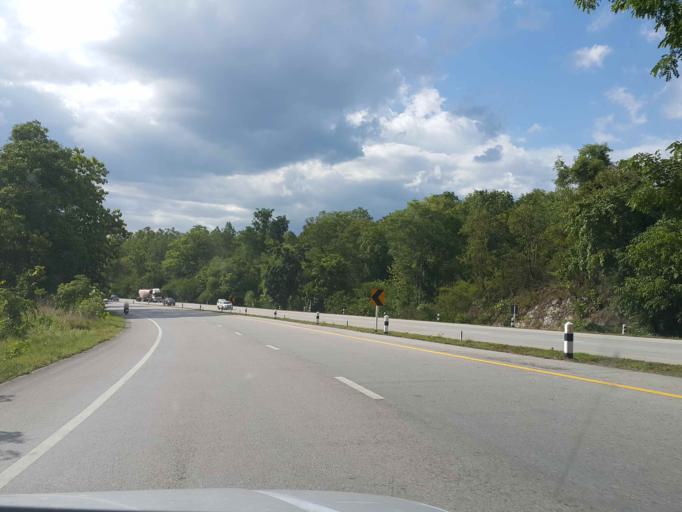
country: TH
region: Lampang
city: Thoen
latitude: 17.6856
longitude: 99.2393
